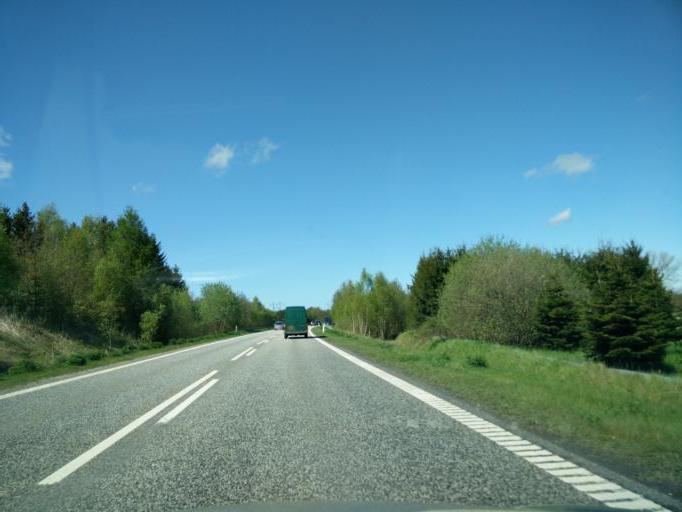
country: DK
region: Capital Region
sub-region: Gribskov Kommune
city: Helsinge
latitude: 55.9992
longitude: 12.2403
